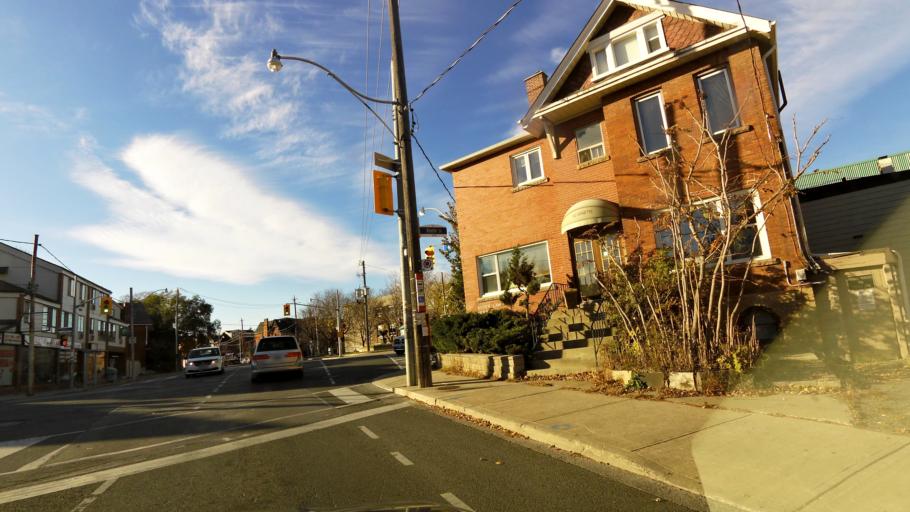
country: CA
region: Ontario
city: Toronto
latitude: 43.6636
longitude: -79.4635
